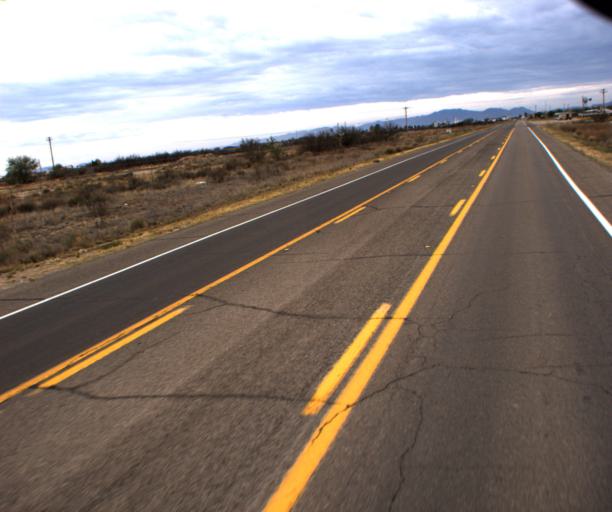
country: US
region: Arizona
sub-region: Cochise County
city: Willcox
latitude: 32.2694
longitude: -109.8210
